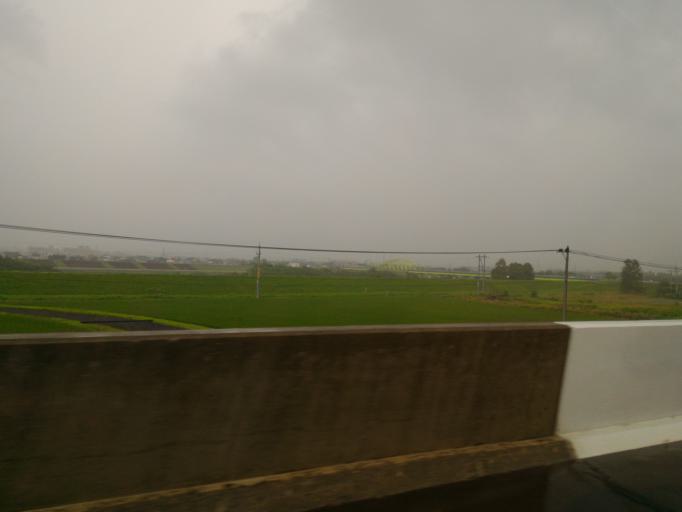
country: JP
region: Hokkaido
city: Nayoro
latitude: 44.3490
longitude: 142.4357
